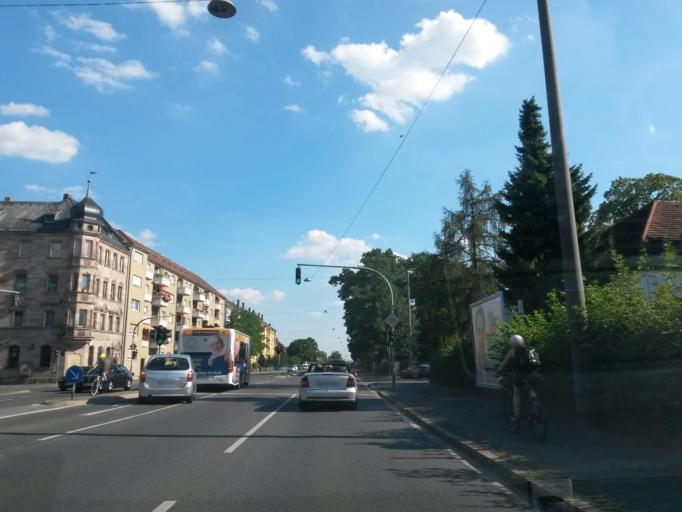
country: DE
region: Bavaria
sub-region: Regierungsbezirk Mittelfranken
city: Furth
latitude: 49.4596
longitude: 10.9878
